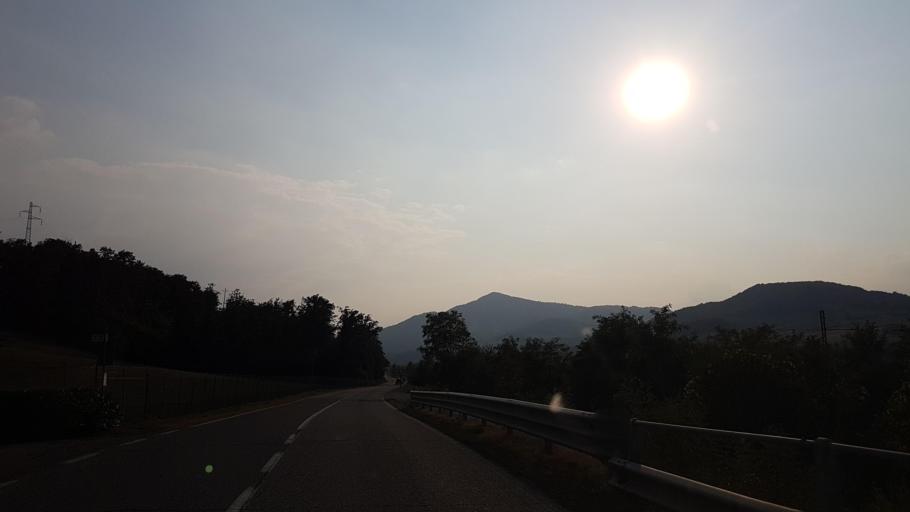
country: IT
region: Emilia-Romagna
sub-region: Provincia di Parma
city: Ramiola
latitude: 44.6623
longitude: 10.0669
